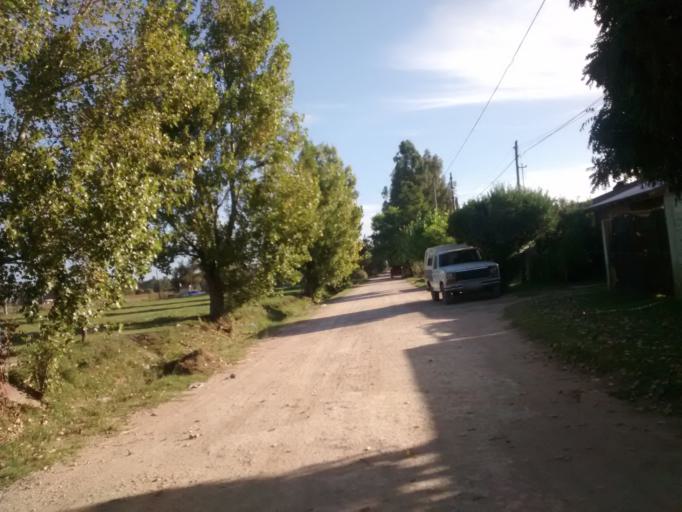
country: AR
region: Buenos Aires
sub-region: Partido de Loberia
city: Loberia
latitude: -38.1710
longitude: -58.7848
